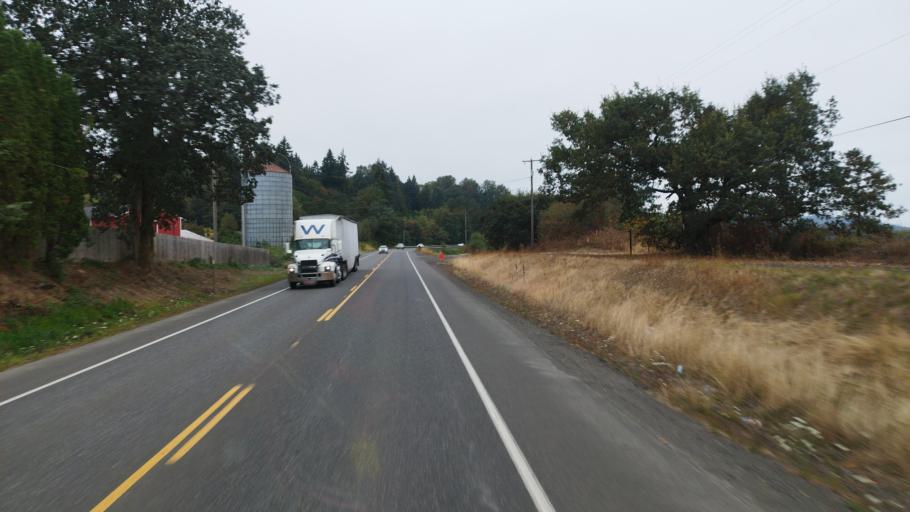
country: US
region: Washington
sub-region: Cowlitz County
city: Kalama
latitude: 45.9428
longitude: -122.8566
